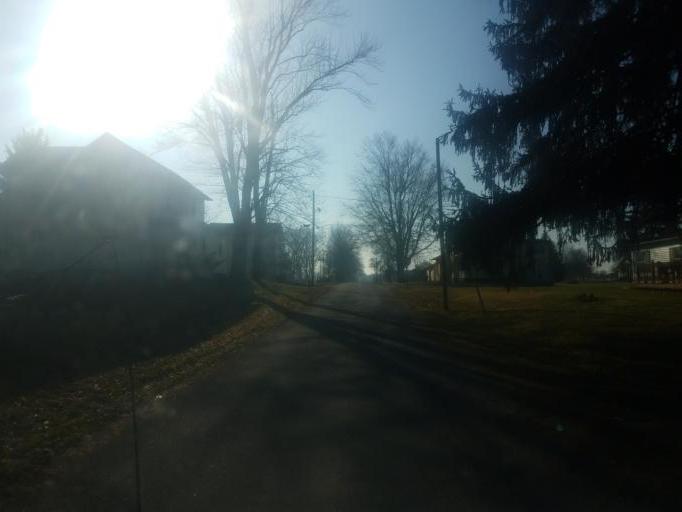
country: US
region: Ohio
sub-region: Seneca County
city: Tiffin
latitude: 41.0498
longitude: -83.0106
